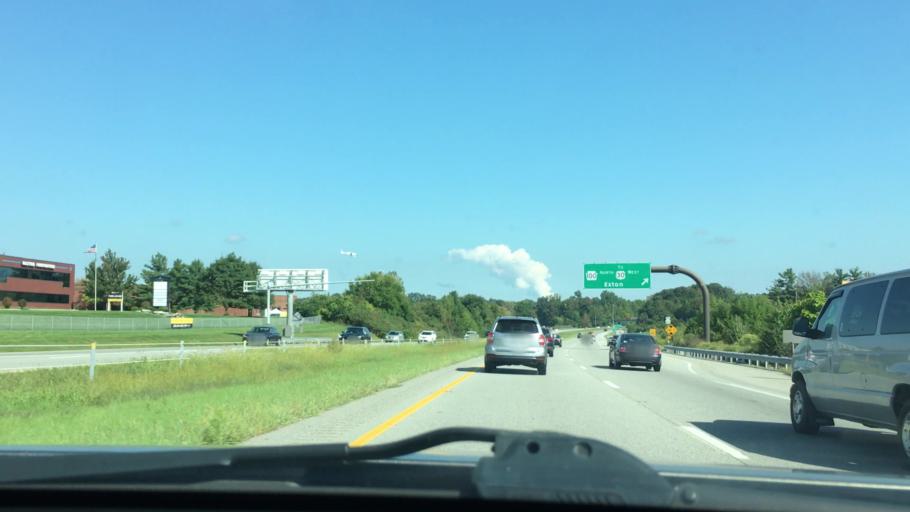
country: US
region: Pennsylvania
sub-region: Chester County
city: West Chester
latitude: 39.9849
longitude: -75.5896
